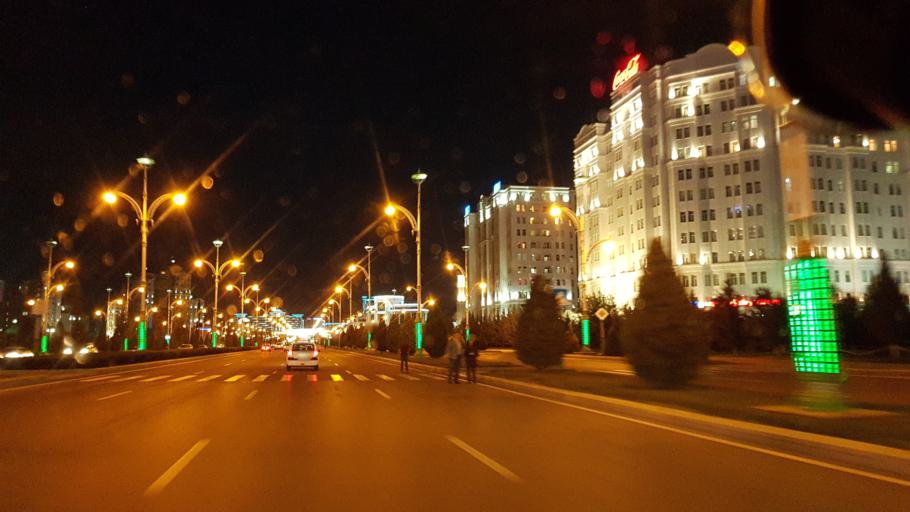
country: TM
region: Ahal
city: Ashgabat
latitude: 37.8992
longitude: 58.3535
